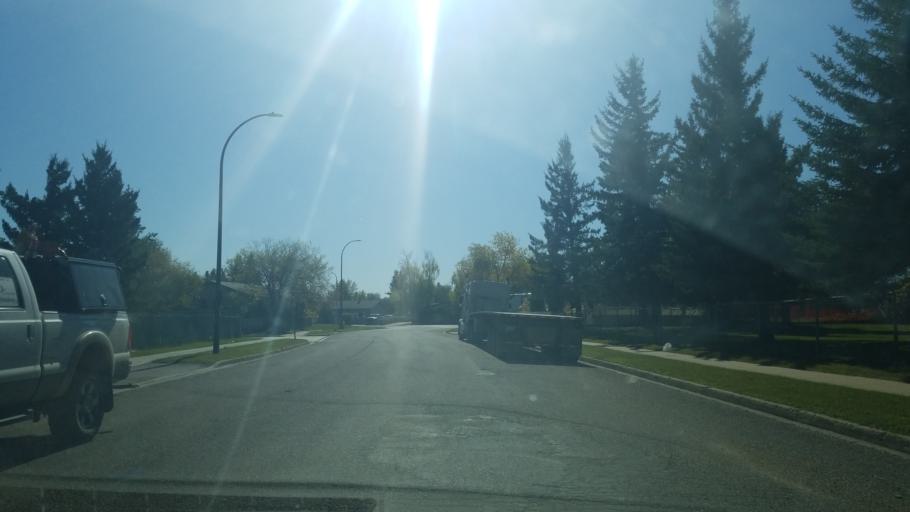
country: CA
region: Saskatchewan
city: Lloydminster
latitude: 53.2739
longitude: -110.0196
